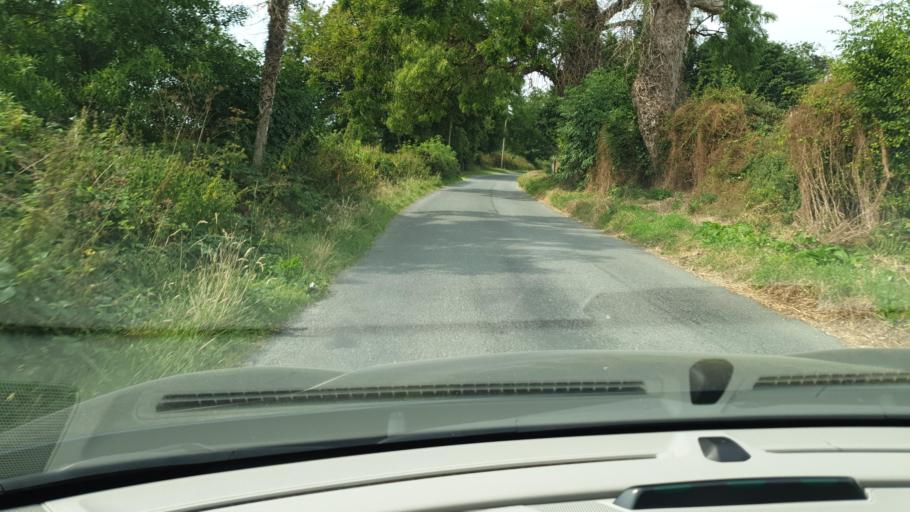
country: IE
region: Leinster
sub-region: An Mhi
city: Athboy
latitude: 53.6588
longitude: -6.9414
